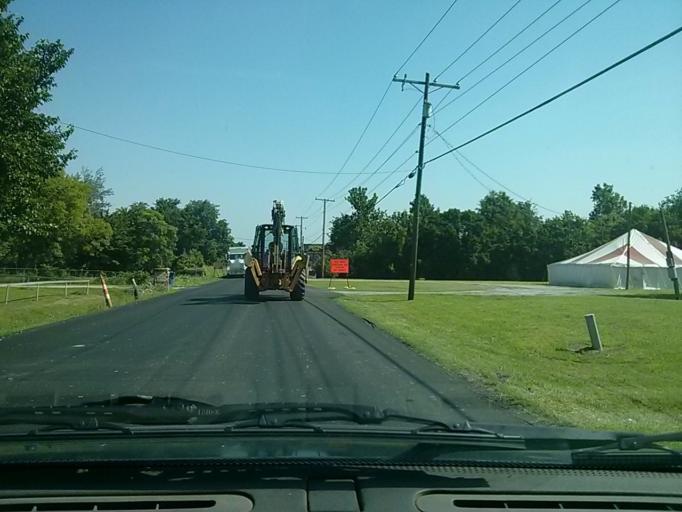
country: US
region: Oklahoma
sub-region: Rogers County
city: Catoosa
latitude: 36.1533
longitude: -95.7617
